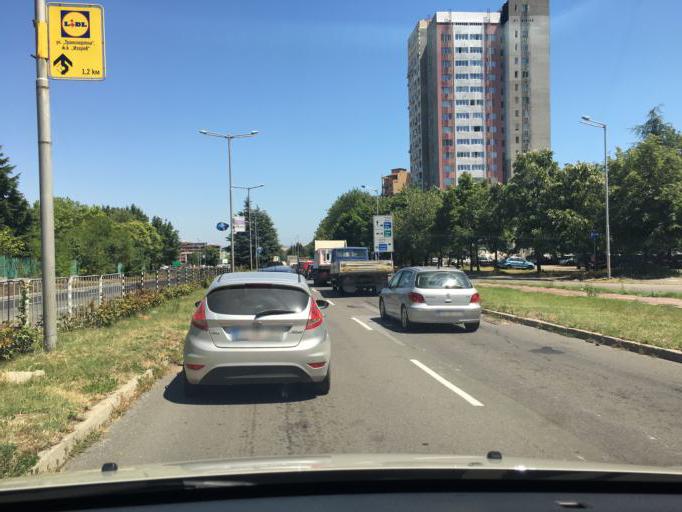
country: BG
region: Burgas
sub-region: Obshtina Burgas
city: Burgas
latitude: 42.5257
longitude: 27.4497
